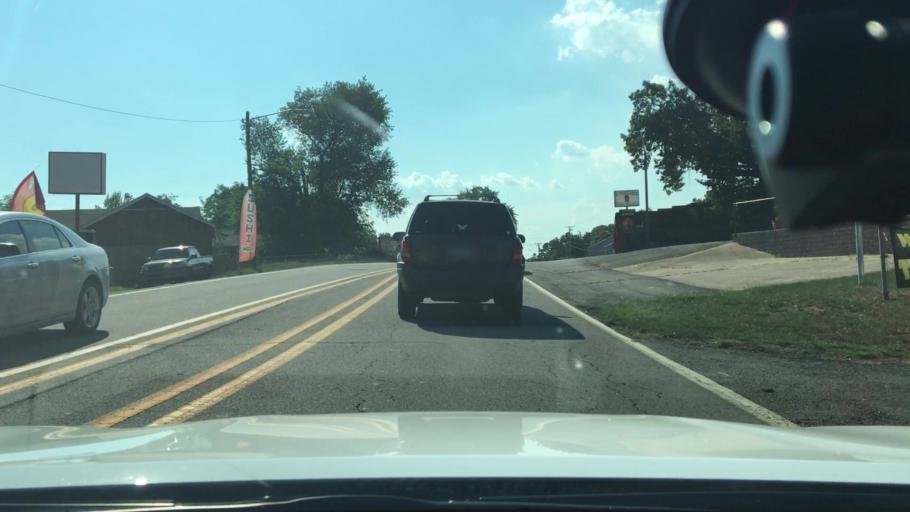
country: US
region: Arkansas
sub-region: Johnson County
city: Clarksville
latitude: 35.4718
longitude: -93.4813
